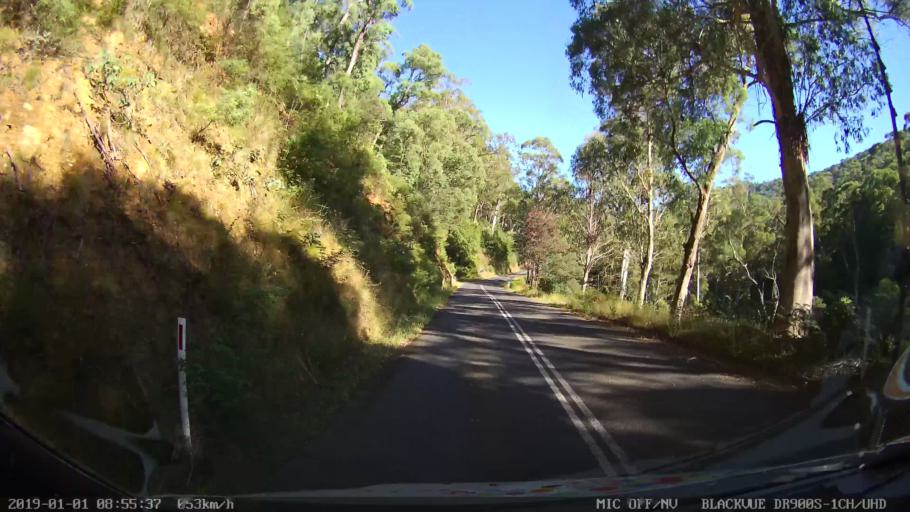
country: AU
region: New South Wales
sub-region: Snowy River
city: Jindabyne
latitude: -36.2526
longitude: 148.1912
